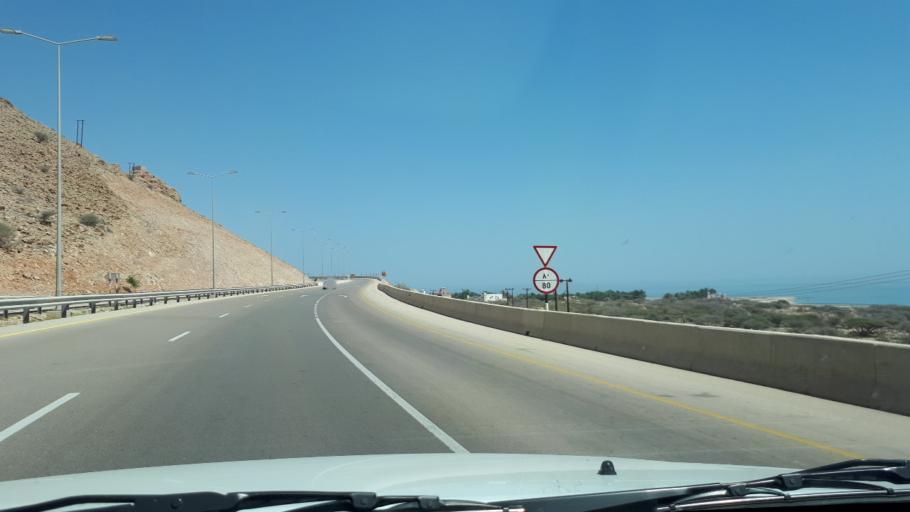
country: OM
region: Ash Sharqiyah
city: Sur
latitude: 22.8170
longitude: 59.2629
